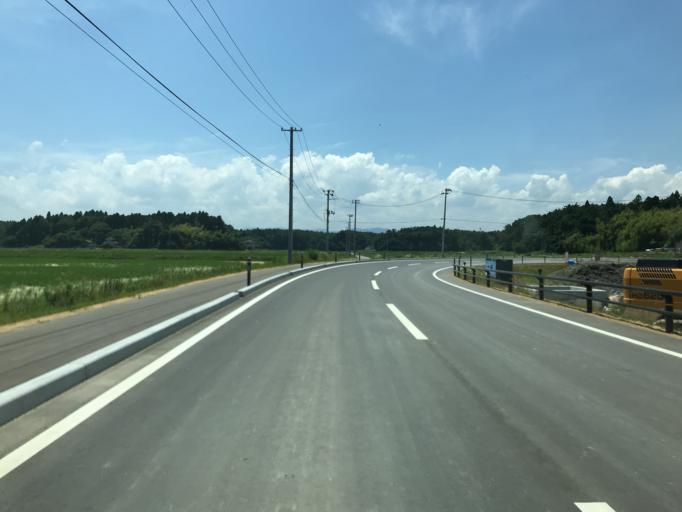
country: JP
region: Fukushima
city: Namie
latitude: 37.7196
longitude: 140.9995
